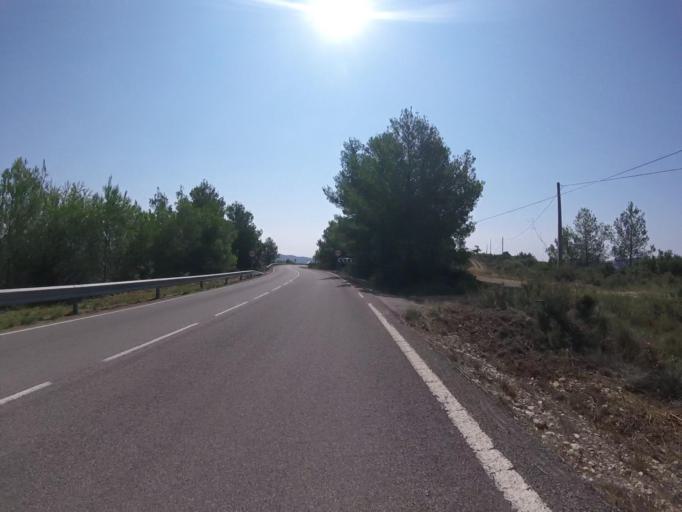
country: ES
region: Valencia
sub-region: Provincia de Castello
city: Benafigos
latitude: 40.2442
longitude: -0.1940
